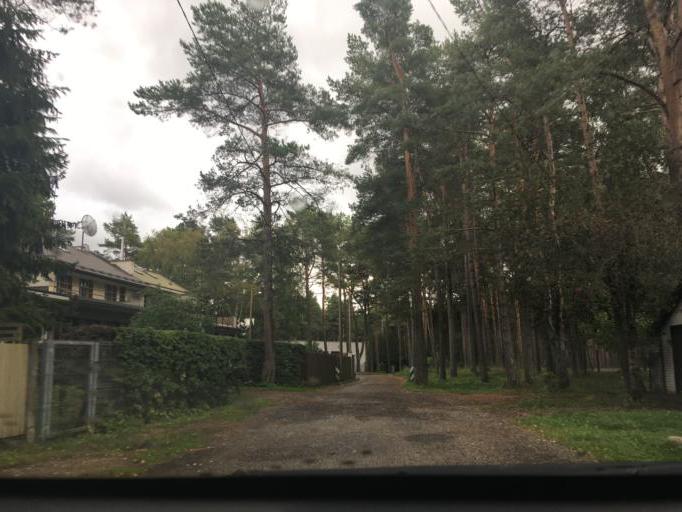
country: EE
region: Harju
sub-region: Saue vald
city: Laagri
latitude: 59.3657
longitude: 24.6531
